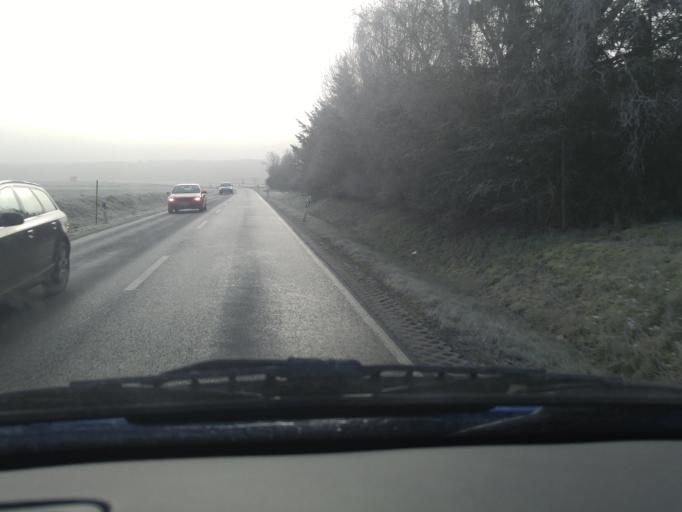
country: DE
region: Hesse
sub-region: Regierungsbezirk Darmstadt
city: Rosbach vor der Hohe
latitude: 50.2655
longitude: 8.7191
